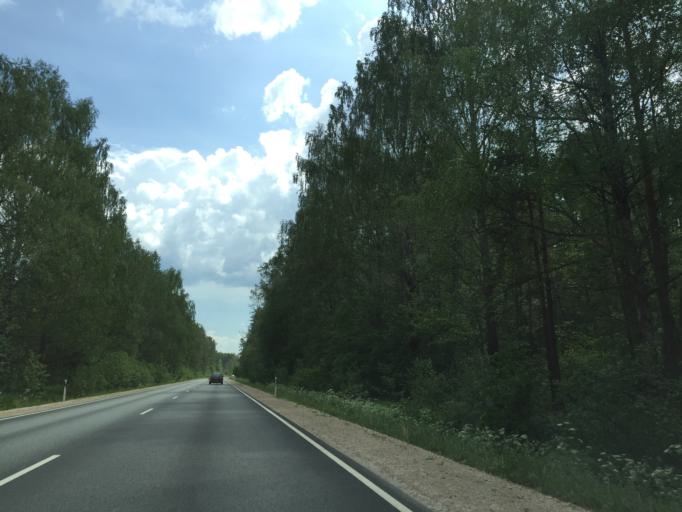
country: LV
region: Ikskile
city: Ikskile
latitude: 56.8906
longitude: 24.4766
